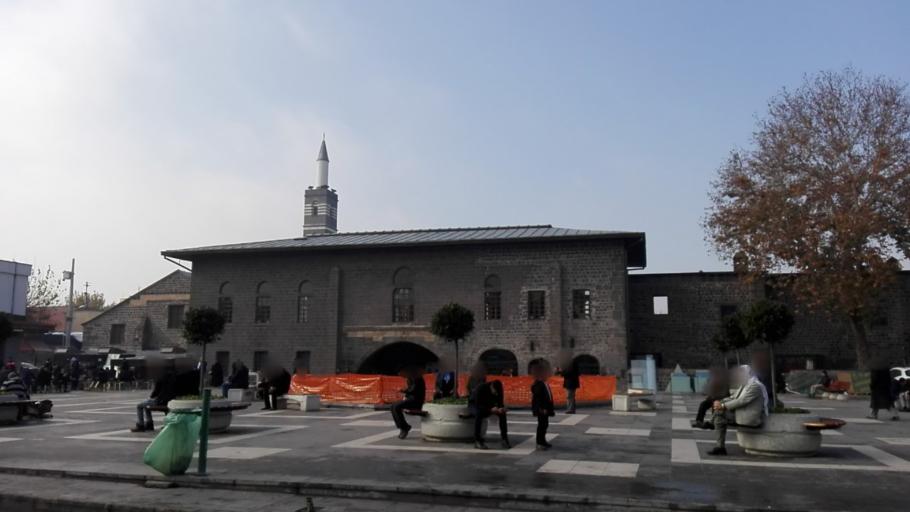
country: TR
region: Diyarbakir
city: Sur
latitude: 37.9126
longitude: 40.2357
